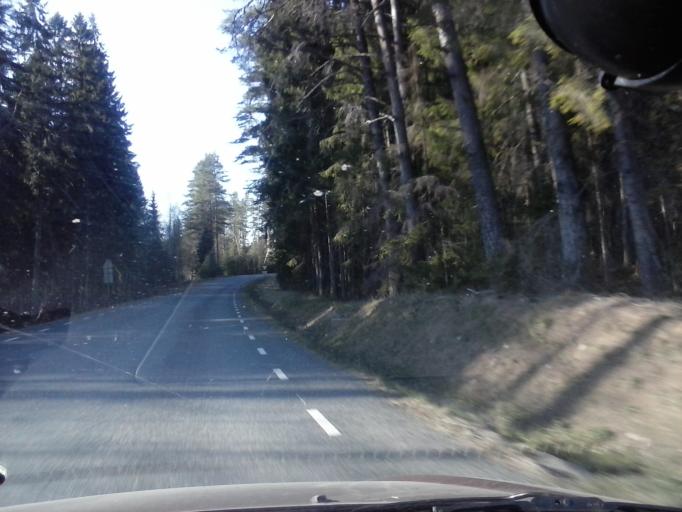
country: EE
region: Tartu
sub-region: UElenurme vald
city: Ulenurme
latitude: 58.1780
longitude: 26.8290
